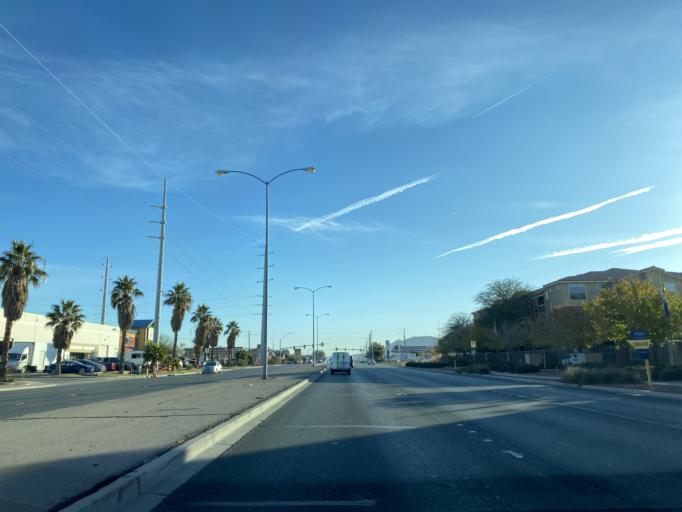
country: US
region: Nevada
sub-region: Clark County
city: Nellis Air Force Base
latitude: 36.2404
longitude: -115.0825
